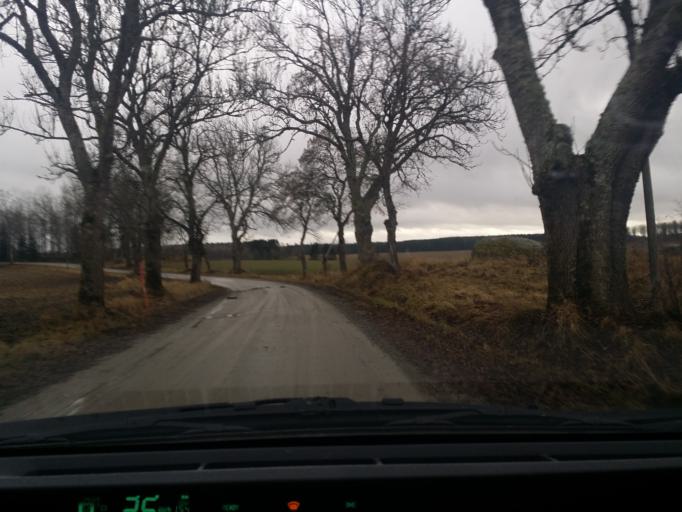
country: SE
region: Vaestmanland
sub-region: Vasteras
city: Skultuna
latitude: 59.7801
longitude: 16.3931
